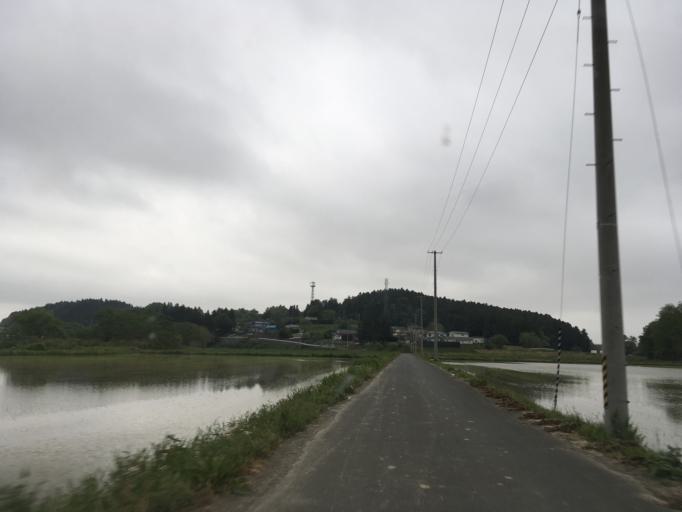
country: JP
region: Miyagi
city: Wakuya
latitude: 38.7124
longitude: 141.2861
